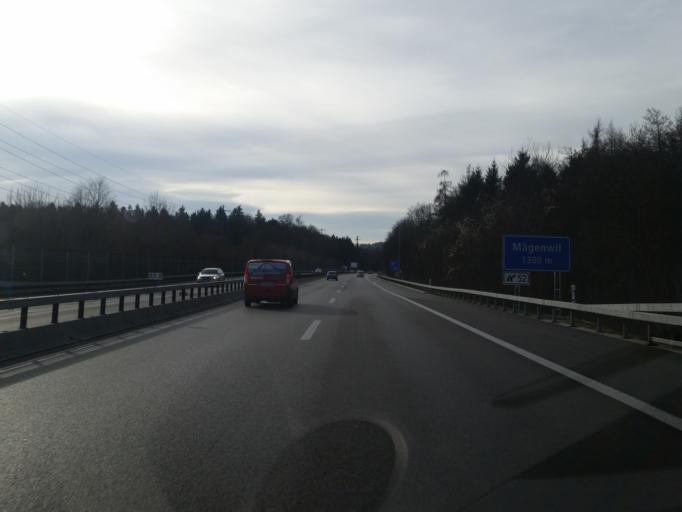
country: CH
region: Aargau
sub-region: Bezirk Baden
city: Birmenstorf
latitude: 47.4328
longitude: 8.2384
